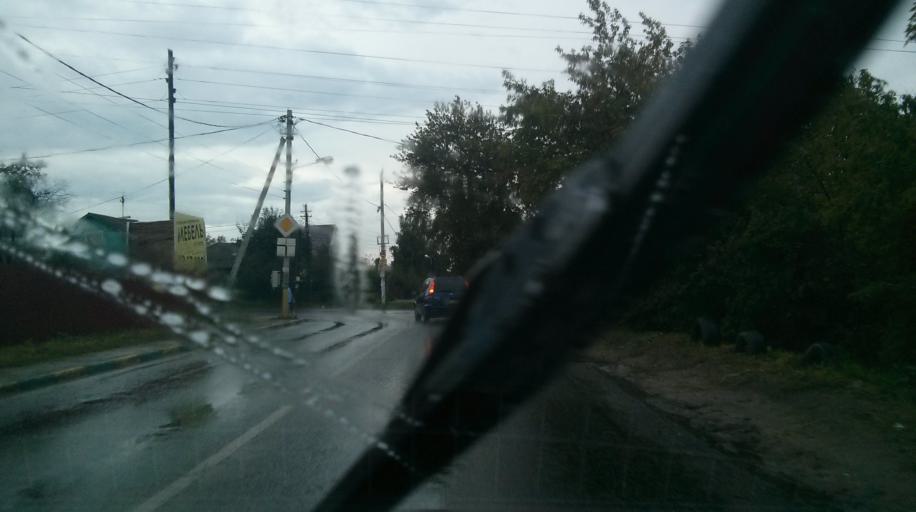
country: RU
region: Nizjnij Novgorod
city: Nizhniy Novgorod
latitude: 56.2567
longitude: 43.9934
